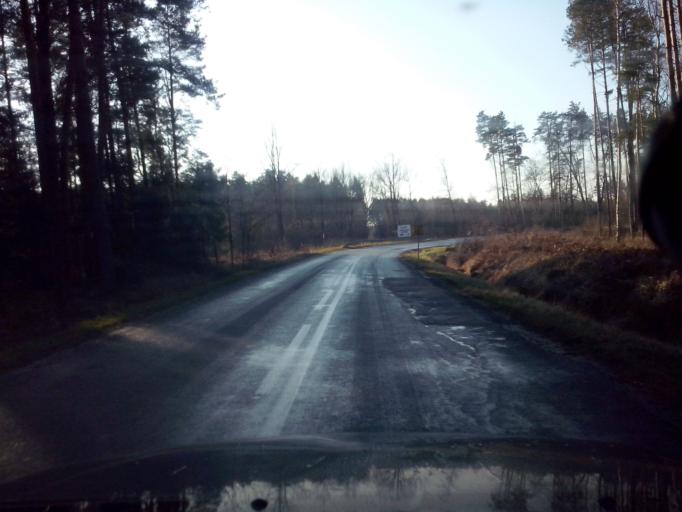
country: PL
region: Subcarpathian Voivodeship
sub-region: Powiat lezajski
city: Letownia
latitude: 50.3653
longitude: 22.2454
